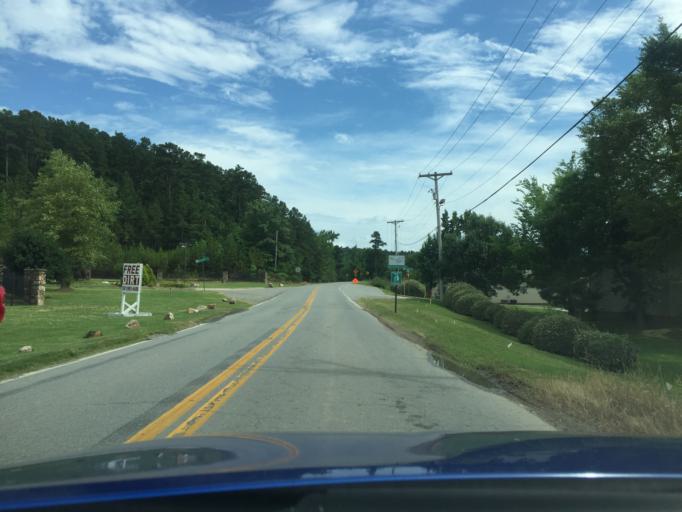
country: US
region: Arkansas
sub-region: Pulaski County
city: Maumelle
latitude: 34.8132
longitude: -92.4432
